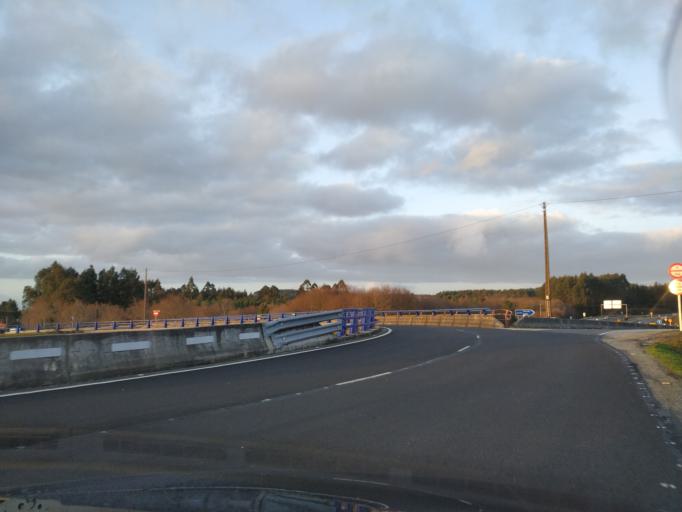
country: ES
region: Galicia
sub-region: Provincia da Coruna
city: Oroso
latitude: 42.9096
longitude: -8.4323
